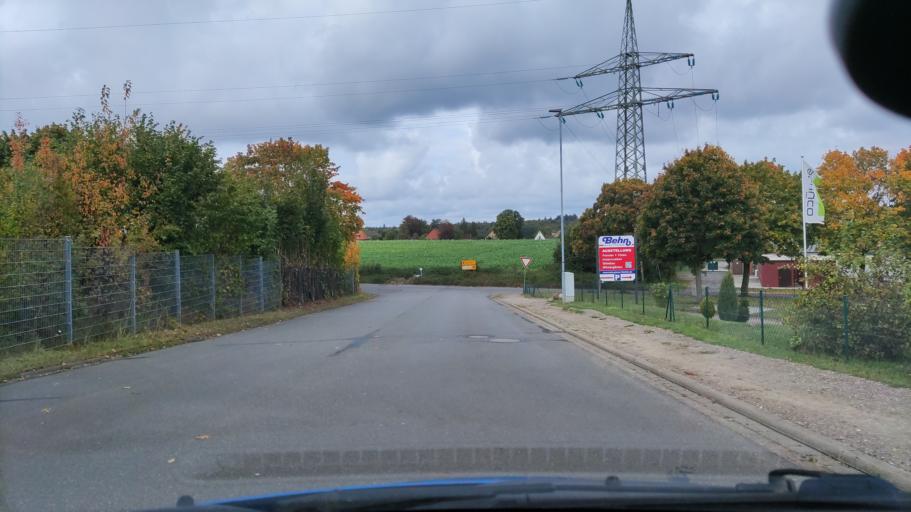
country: DE
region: Lower Saxony
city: Bad Bevensen
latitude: 53.0724
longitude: 10.5696
